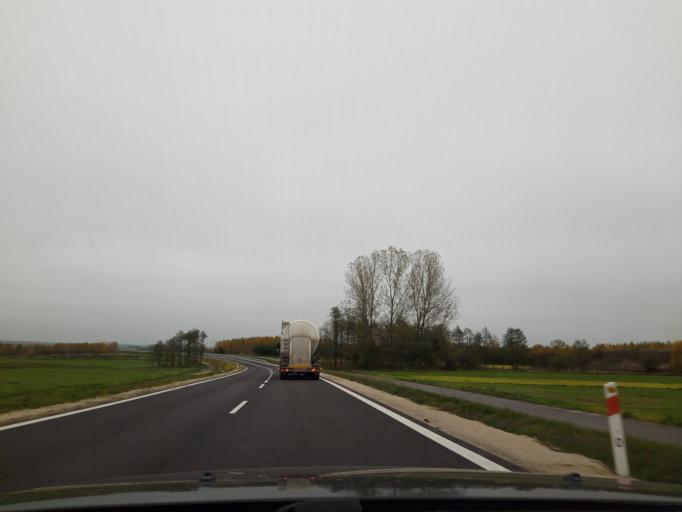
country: PL
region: Swietokrzyskie
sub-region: Powiat jedrzejowski
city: Jedrzejow
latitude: 50.6236
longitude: 20.3217
